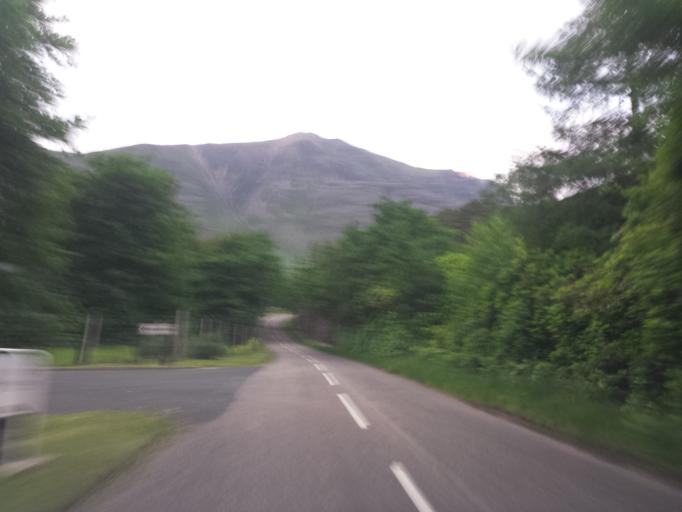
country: GB
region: Scotland
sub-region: Highland
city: Ullapool
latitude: 57.5280
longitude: -5.5260
